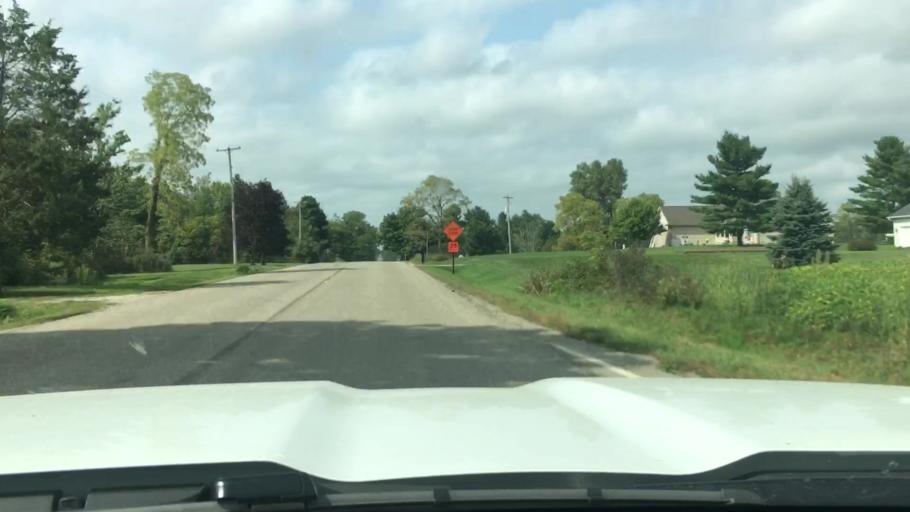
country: US
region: Michigan
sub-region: Eaton County
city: Dimondale
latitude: 42.6256
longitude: -84.6817
